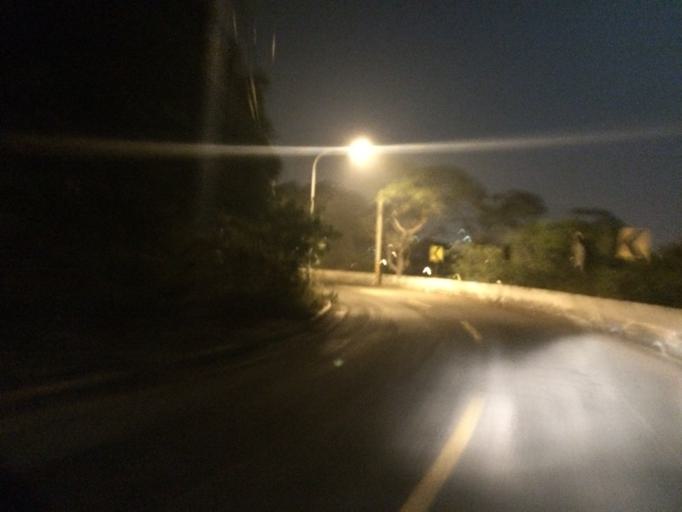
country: TW
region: Taiwan
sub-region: Hsinchu
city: Hsinchu
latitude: 24.7266
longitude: 120.9003
